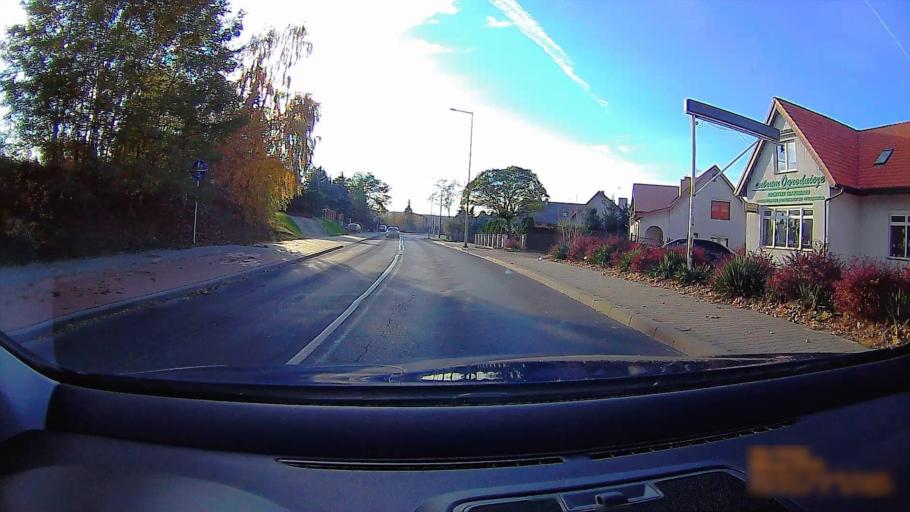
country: PL
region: Greater Poland Voivodeship
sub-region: Konin
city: Konin
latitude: 52.2034
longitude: 18.2315
